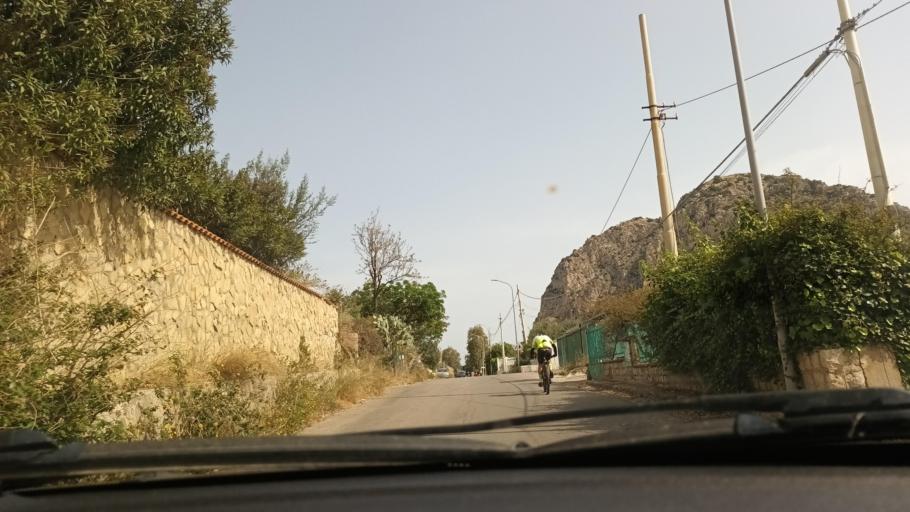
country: IT
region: Sicily
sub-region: Palermo
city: Santa Flavia
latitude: 38.1046
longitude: 13.5330
